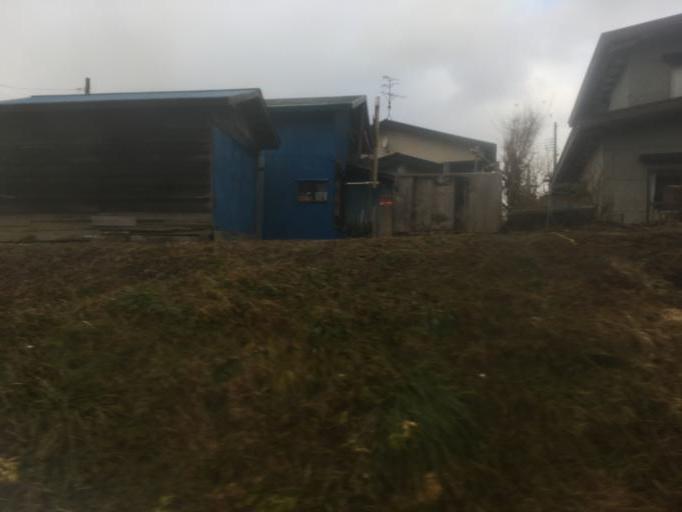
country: JP
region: Aomori
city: Goshogawara
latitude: 41.1823
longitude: 140.4844
